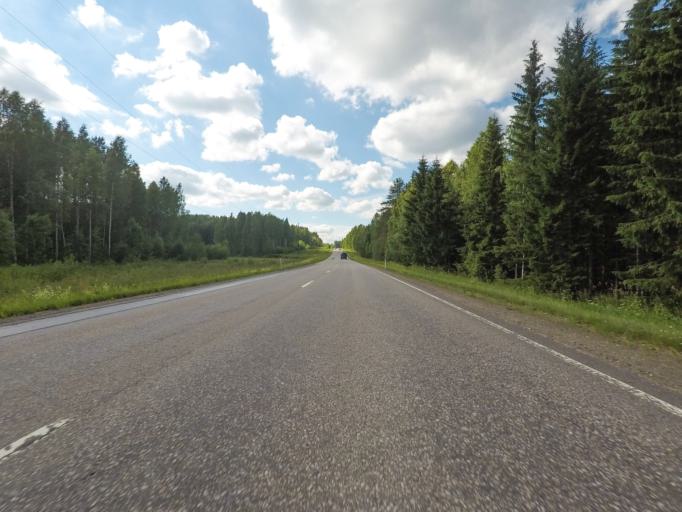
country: FI
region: Southern Savonia
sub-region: Savonlinna
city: Kerimaeki
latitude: 61.8414
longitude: 29.2094
